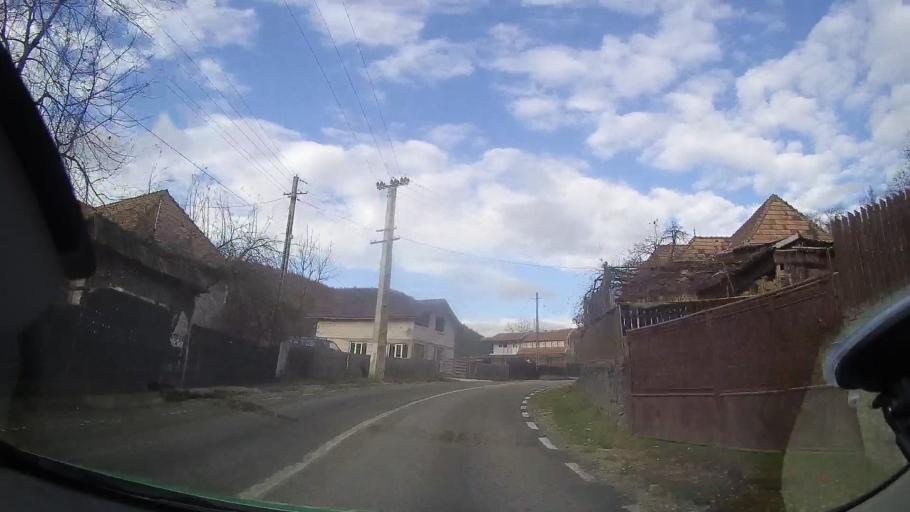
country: RO
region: Cluj
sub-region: Comuna Baisoara
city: Baisoara
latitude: 46.5812
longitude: 23.4567
